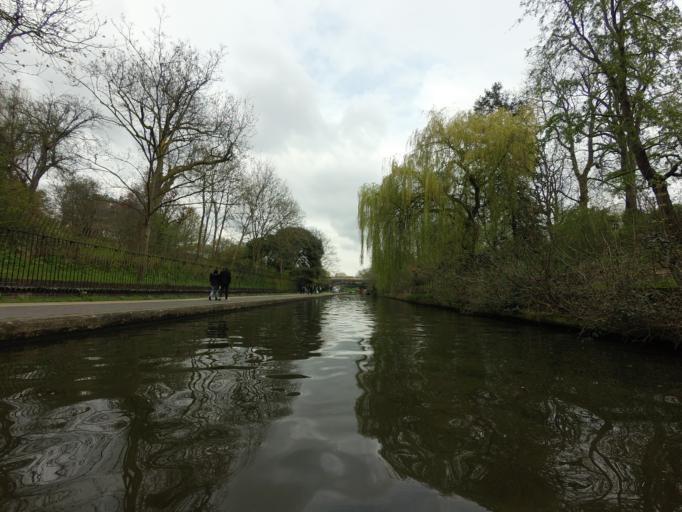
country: GB
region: England
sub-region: Greater London
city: Camden Town
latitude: 51.5368
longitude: -0.1553
